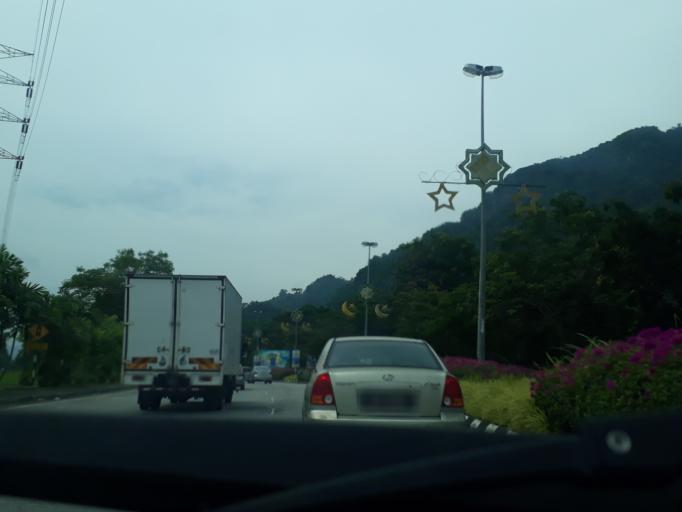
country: MY
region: Perak
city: Ipoh
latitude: 4.6249
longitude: 101.1522
